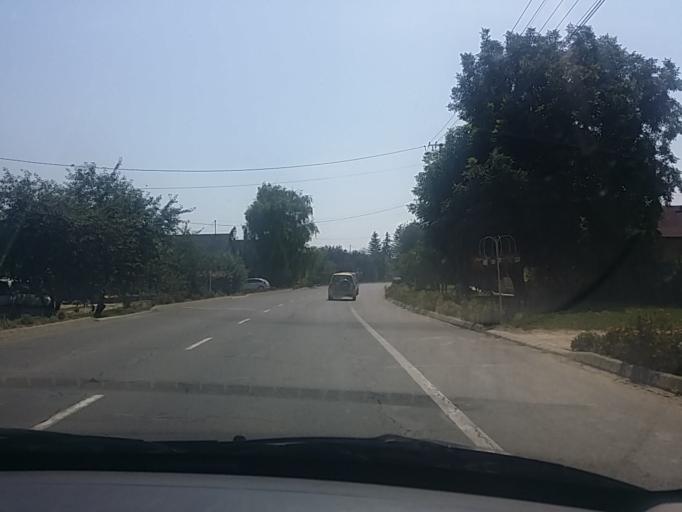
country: HU
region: Tolna
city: Tamasi
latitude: 46.5917
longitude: 18.2032
